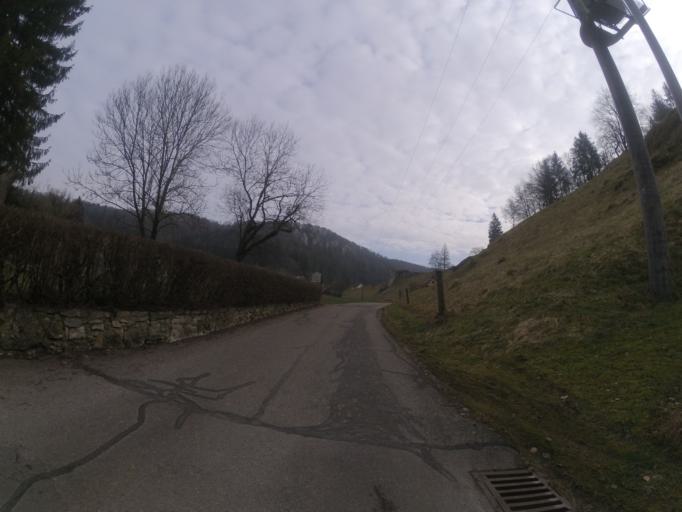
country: DE
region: Baden-Wuerttemberg
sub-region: Tuebingen Region
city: Hayingen
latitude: 48.3230
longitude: 9.4985
